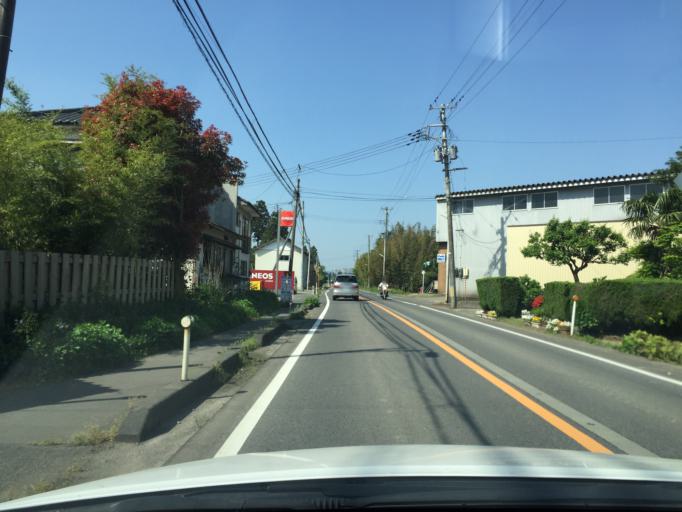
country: JP
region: Niigata
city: Muramatsu
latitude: 37.7053
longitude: 139.1987
